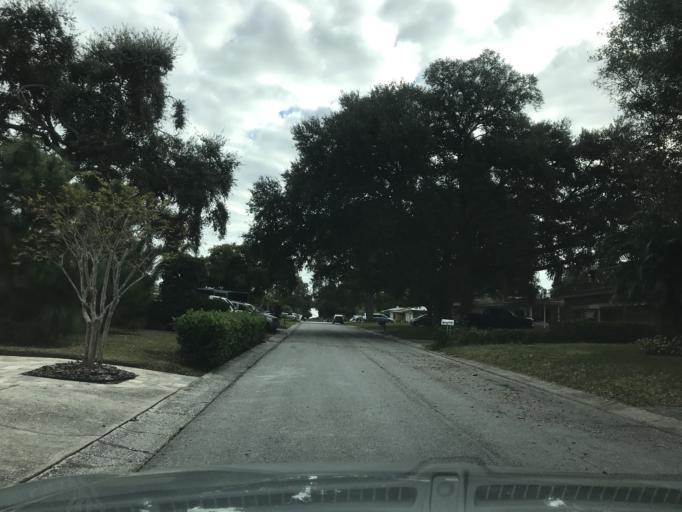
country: US
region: Florida
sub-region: Pinellas County
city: Belleair
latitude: 27.9453
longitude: -82.7786
